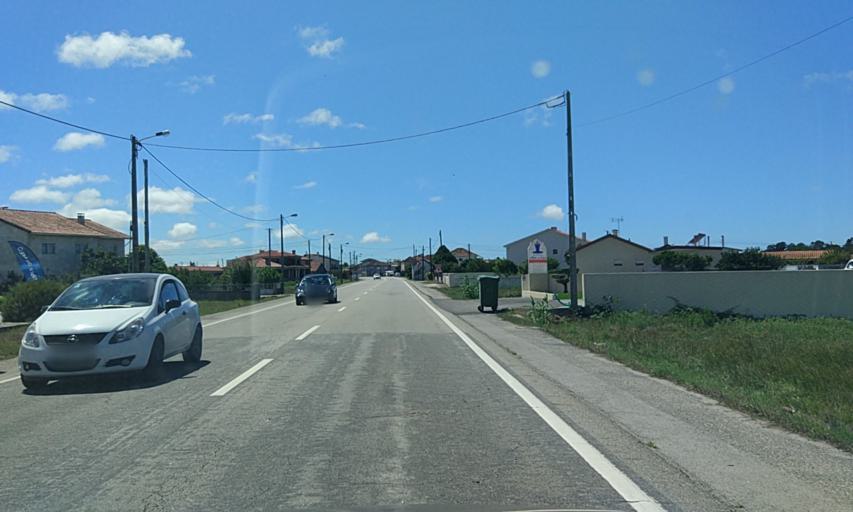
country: PT
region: Coimbra
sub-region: Mira
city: Mira
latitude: 40.4801
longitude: -8.6929
